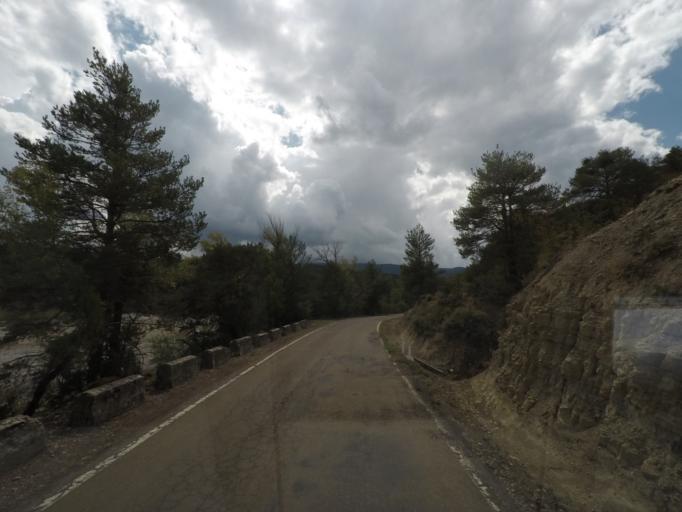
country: ES
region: Aragon
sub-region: Provincia de Huesca
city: Yebra de Basa
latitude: 42.3927
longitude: -0.2705
